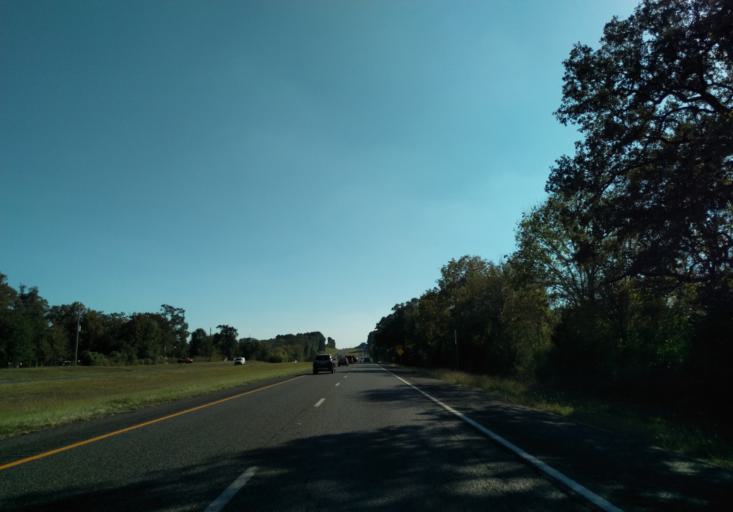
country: US
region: Texas
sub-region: Waller County
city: Hempstead
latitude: 30.2236
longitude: -96.0562
